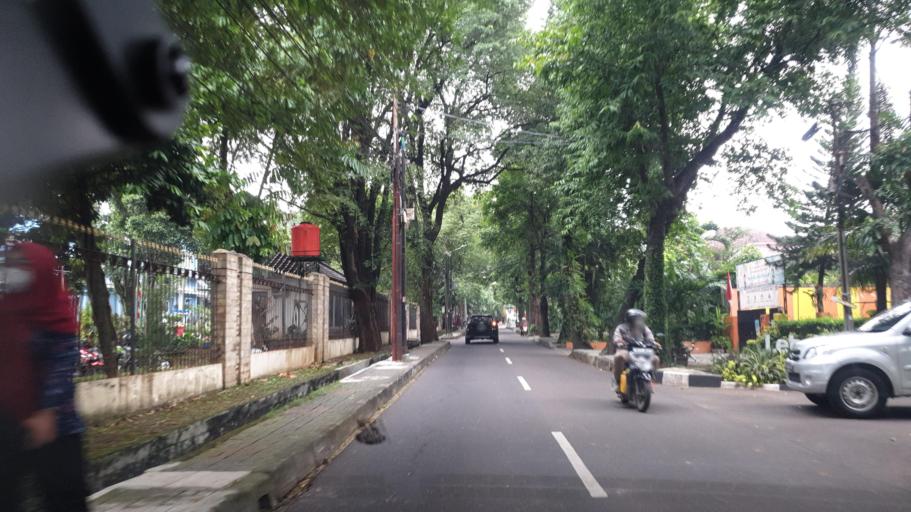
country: ID
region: West Java
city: Pamulang
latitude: -6.3061
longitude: 106.7781
